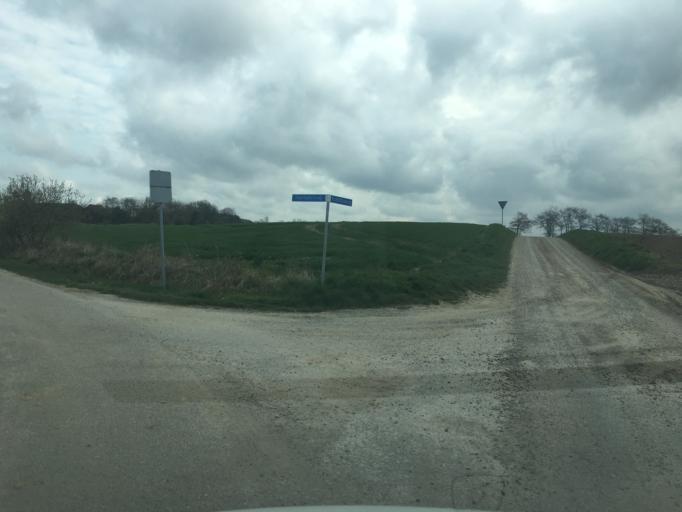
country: DE
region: Schleswig-Holstein
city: Glucksburg
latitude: 54.8972
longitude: 9.5007
